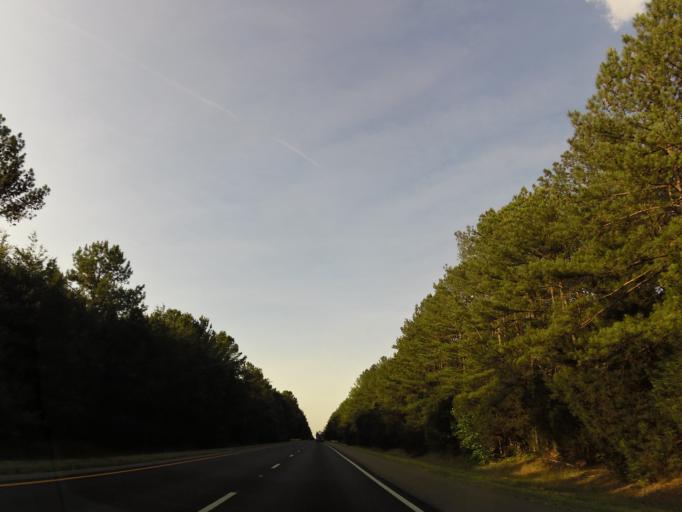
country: US
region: Alabama
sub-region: DeKalb County
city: Fort Payne
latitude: 34.3998
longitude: -85.7829
